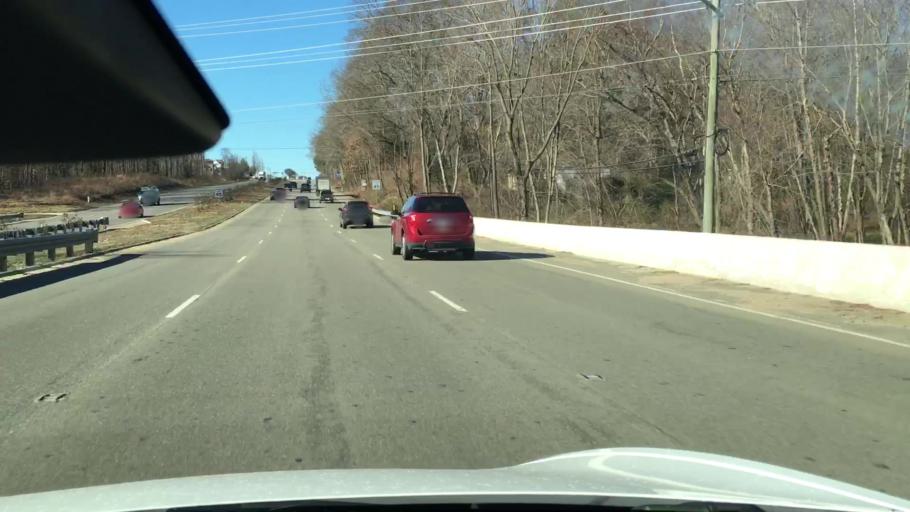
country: US
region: Virginia
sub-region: Chesterfield County
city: Brandermill
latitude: 37.5030
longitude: -77.6322
